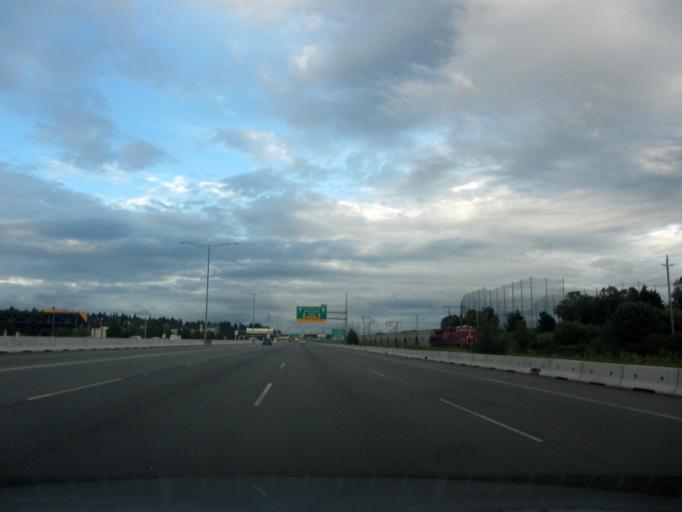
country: CA
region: British Columbia
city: New Westminster
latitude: 49.2333
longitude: -122.8709
